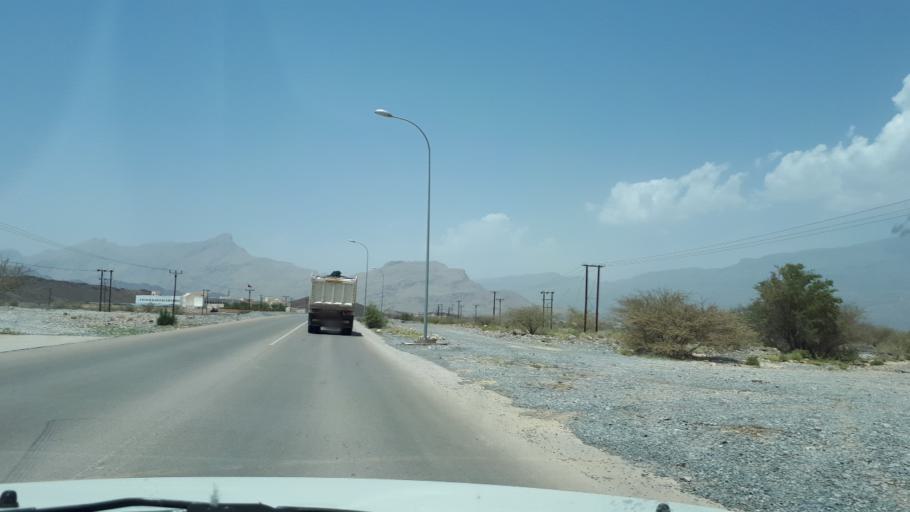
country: OM
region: Muhafazat ad Dakhiliyah
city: Bahla'
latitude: 23.0622
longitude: 57.2799
